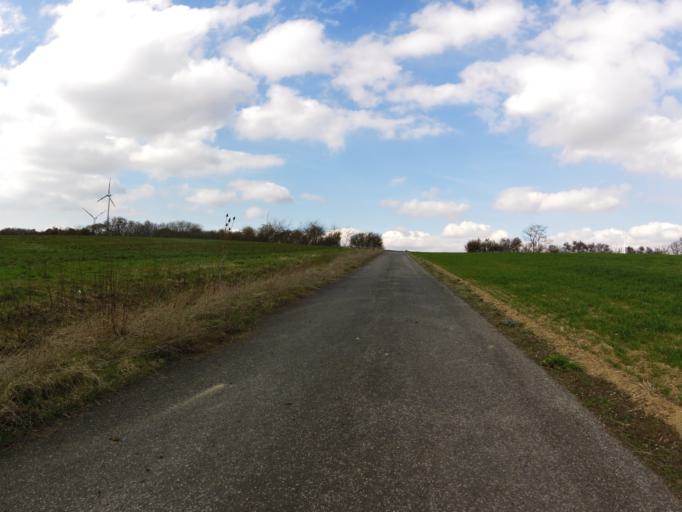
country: DE
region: Bavaria
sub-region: Regierungsbezirk Unterfranken
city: Buchbrunn
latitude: 49.7488
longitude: 10.1141
